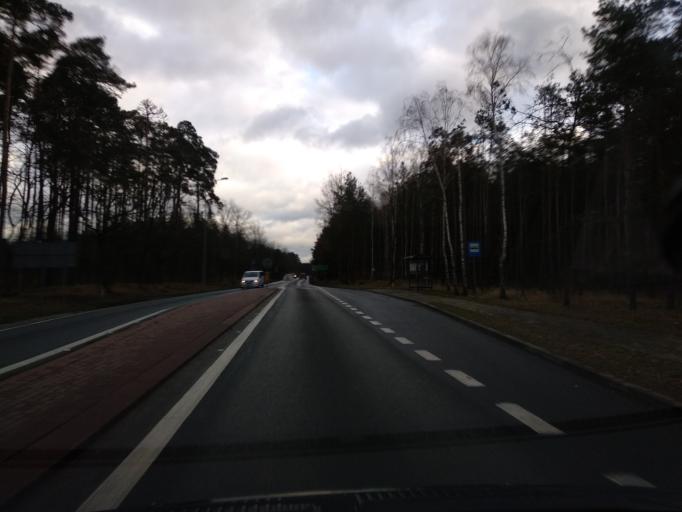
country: PL
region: Greater Poland Voivodeship
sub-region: Powiat ostrowski
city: Jankow Przygodzki
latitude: 51.4954
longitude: 17.7842
